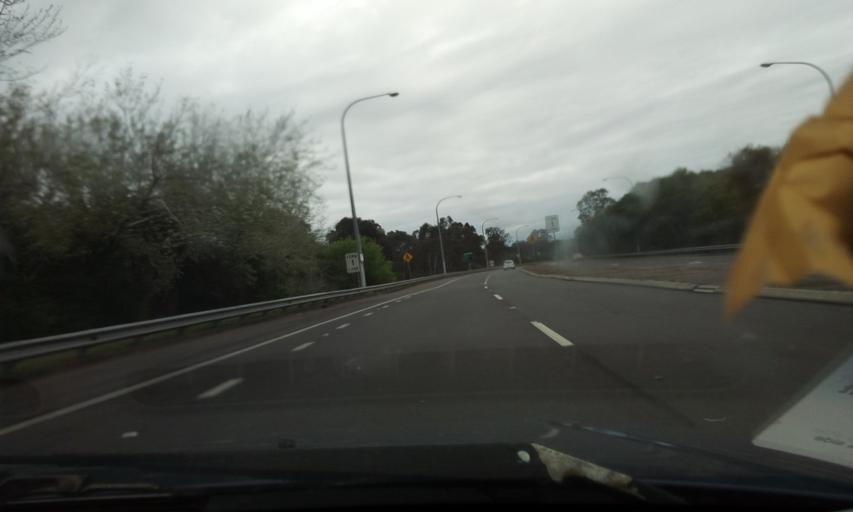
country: AU
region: New South Wales
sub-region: Camden
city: Camden South
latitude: -34.0735
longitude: 150.6963
